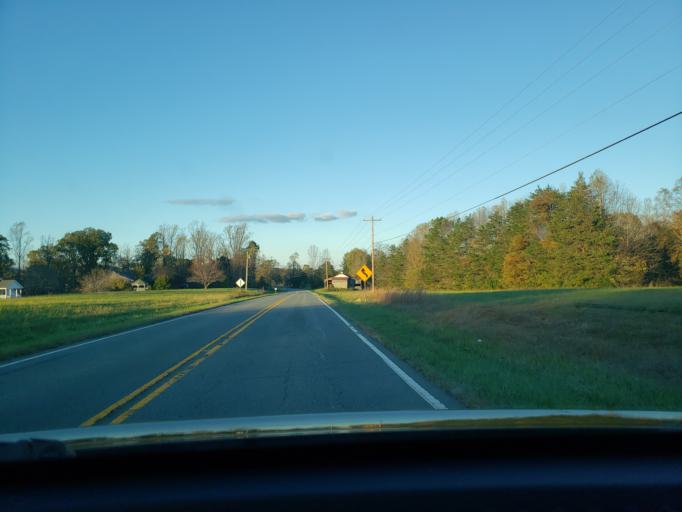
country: US
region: North Carolina
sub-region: Stokes County
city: Danbury
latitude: 36.3260
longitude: -80.2263
